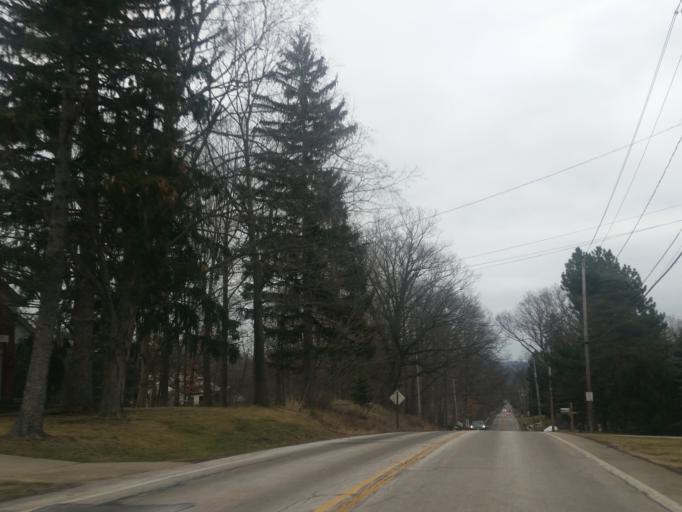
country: US
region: Ohio
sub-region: Cuyahoga County
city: Independence
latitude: 41.3448
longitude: -81.6432
